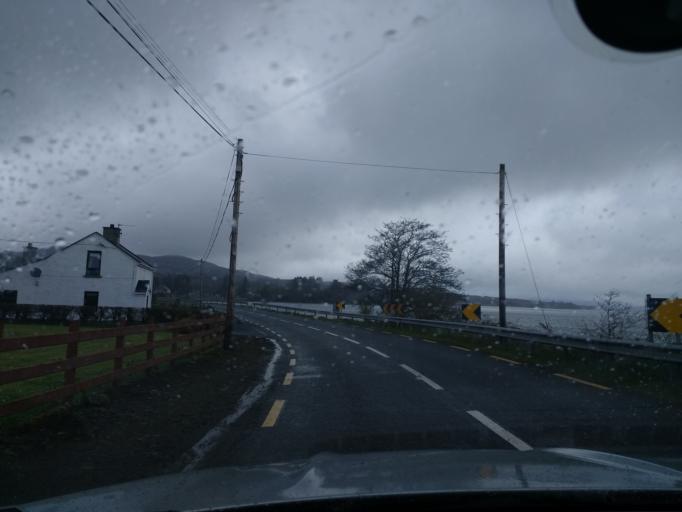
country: IE
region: Ulster
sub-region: County Donegal
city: Ramelton
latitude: 55.0694
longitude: -7.5993
